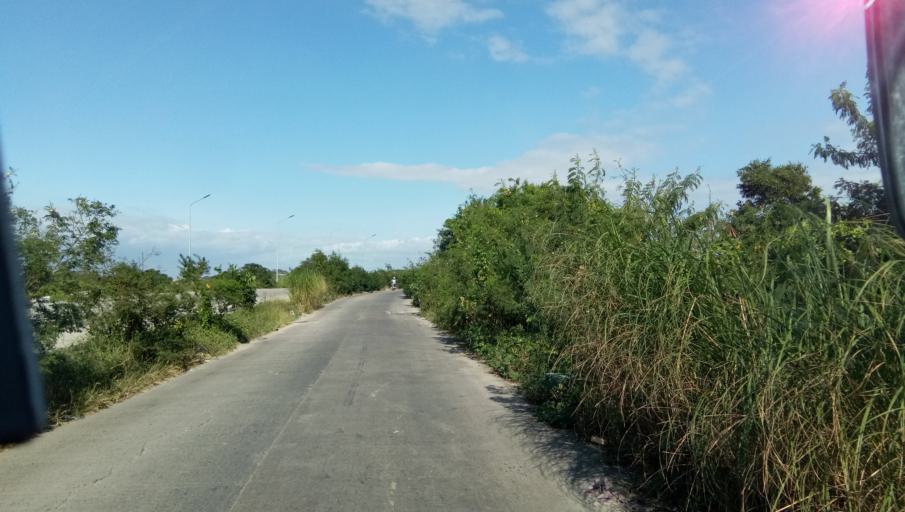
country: PH
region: Calabarzon
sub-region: Province of Cavite
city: Pasong Kawayan Primero
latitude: 14.3617
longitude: 120.9055
